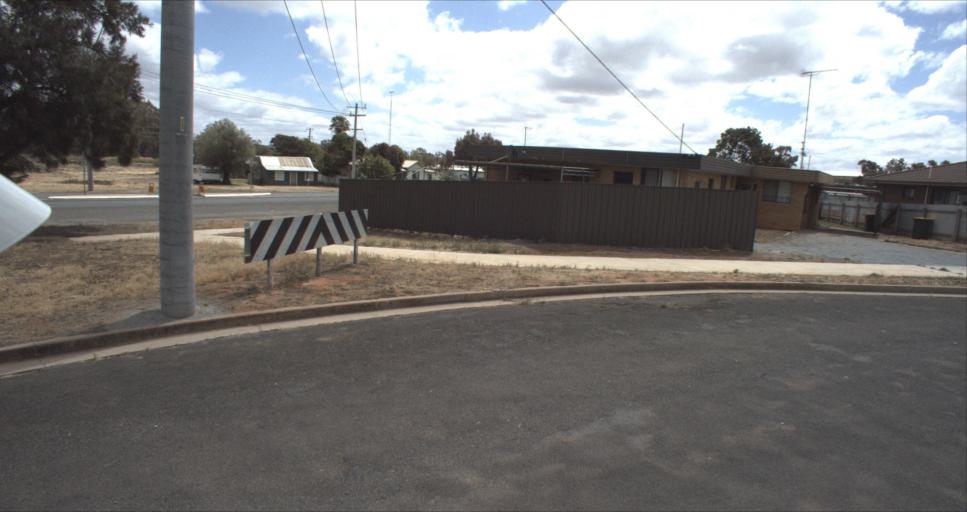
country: AU
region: New South Wales
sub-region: Leeton
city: Leeton
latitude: -34.5619
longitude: 146.3930
